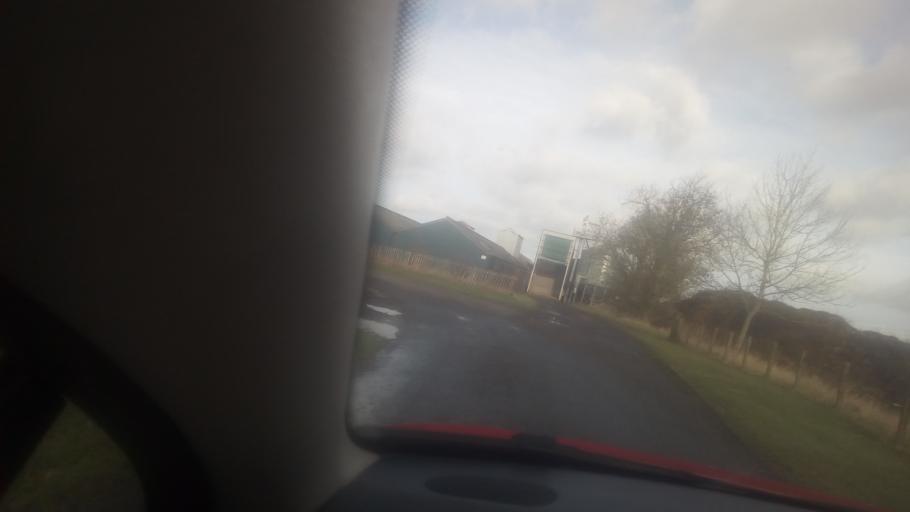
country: GB
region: Scotland
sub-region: The Scottish Borders
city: Kelso
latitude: 55.5032
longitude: -2.4225
